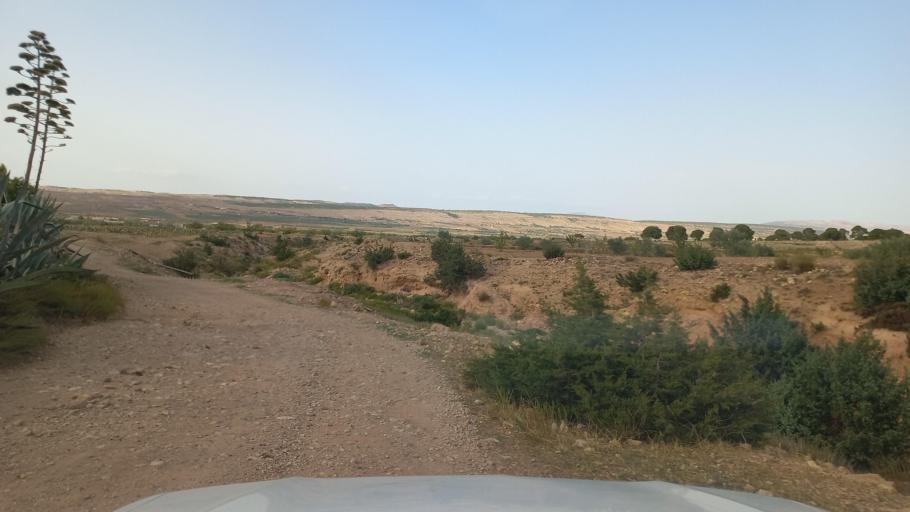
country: TN
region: Al Qasrayn
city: Kasserine
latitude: 35.3350
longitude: 8.8503
